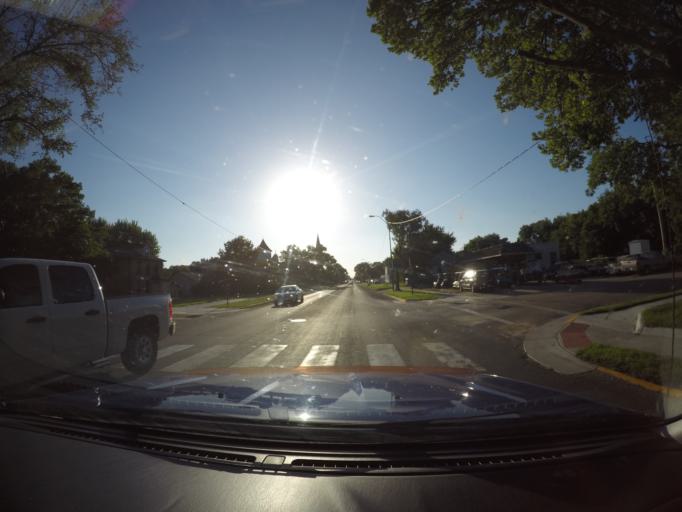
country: US
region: Kansas
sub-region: Pottawatomie County
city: Saint Marys
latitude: 39.1914
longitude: -96.0636
